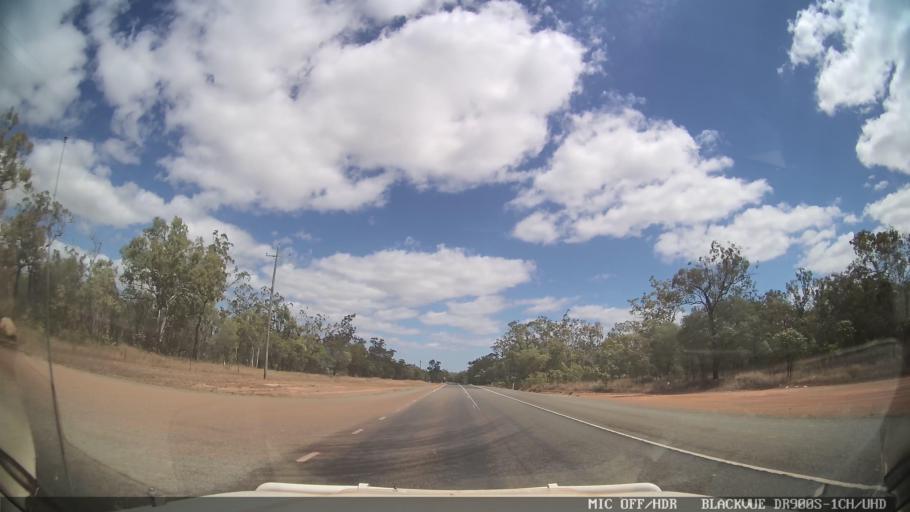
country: AU
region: Queensland
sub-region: Tablelands
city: Ravenshoe
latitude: -17.9111
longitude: 144.8793
